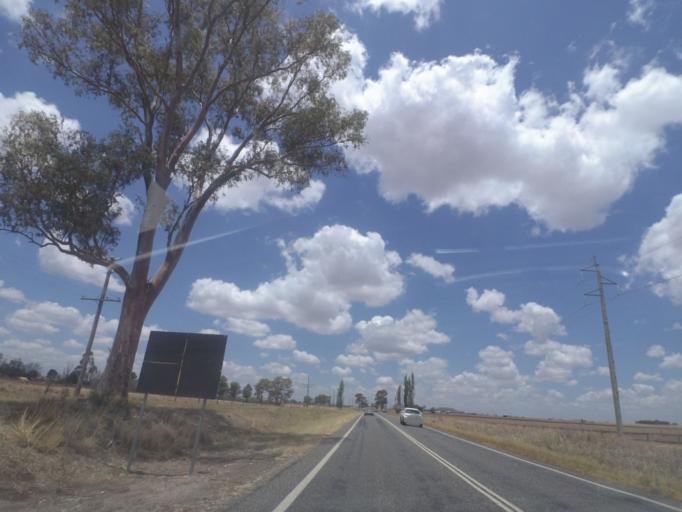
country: AU
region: Queensland
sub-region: Toowoomba
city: Top Camp
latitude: -27.9248
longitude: 151.9840
